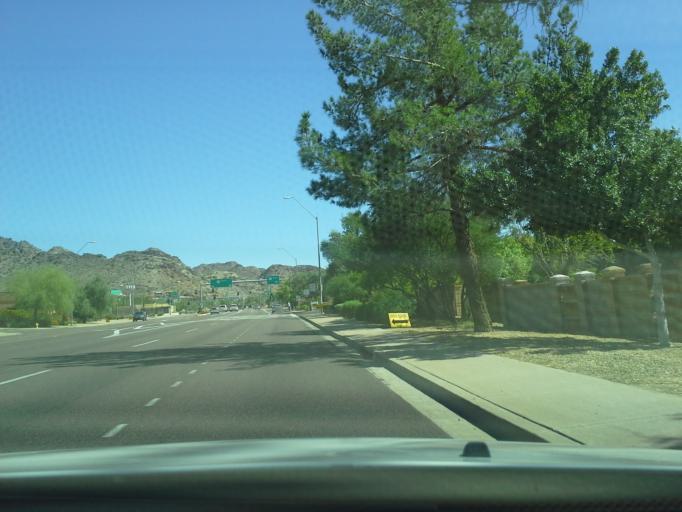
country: US
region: Arizona
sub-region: Maricopa County
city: Phoenix
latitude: 33.5382
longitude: -112.0441
